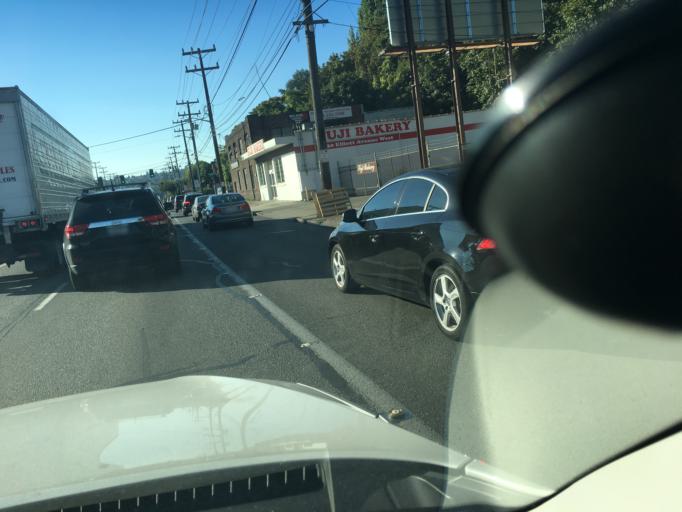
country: US
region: Washington
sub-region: King County
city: Seattle
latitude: 47.6279
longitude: -122.3701
